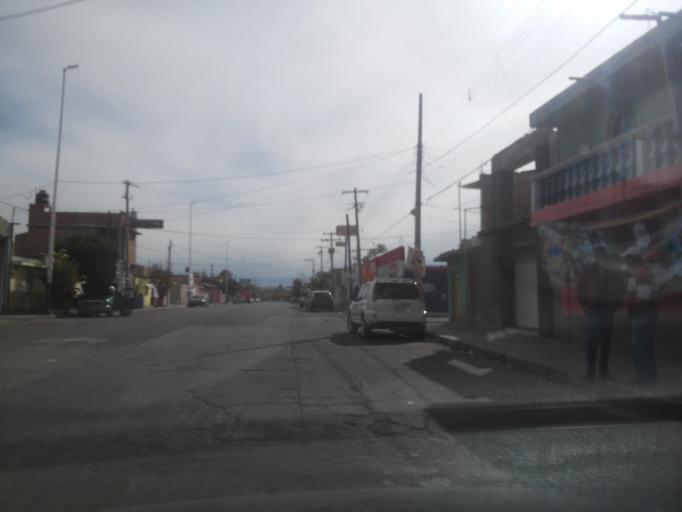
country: MX
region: Durango
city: Victoria de Durango
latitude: 24.0182
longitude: -104.6554
